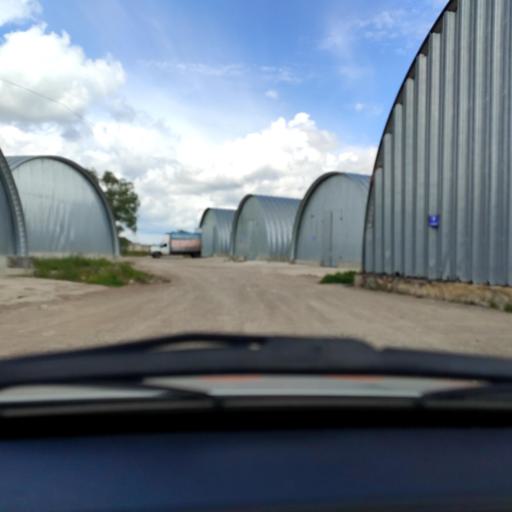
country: RU
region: Bashkortostan
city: Mikhaylovka
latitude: 54.8028
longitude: 55.8512
